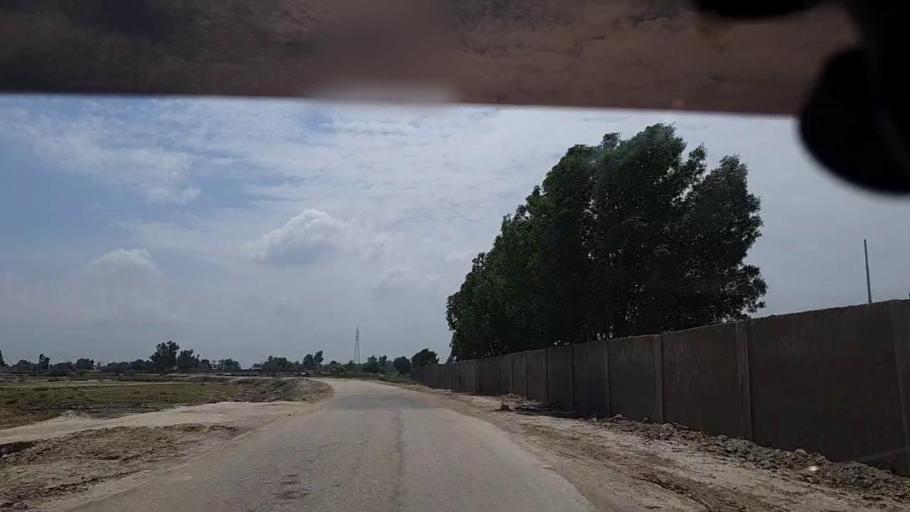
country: PK
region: Sindh
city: Ghauspur
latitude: 28.0916
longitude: 68.9603
